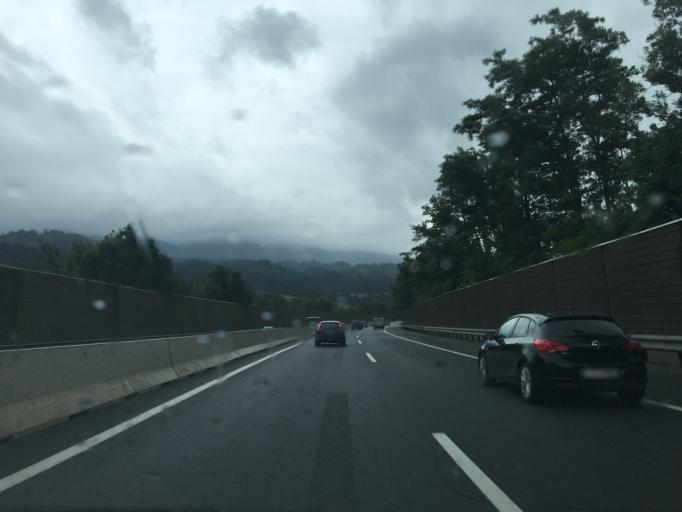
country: AT
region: Tyrol
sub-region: Politischer Bezirk Innsbruck Land
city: Baumkirchen
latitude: 47.2945
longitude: 11.5654
